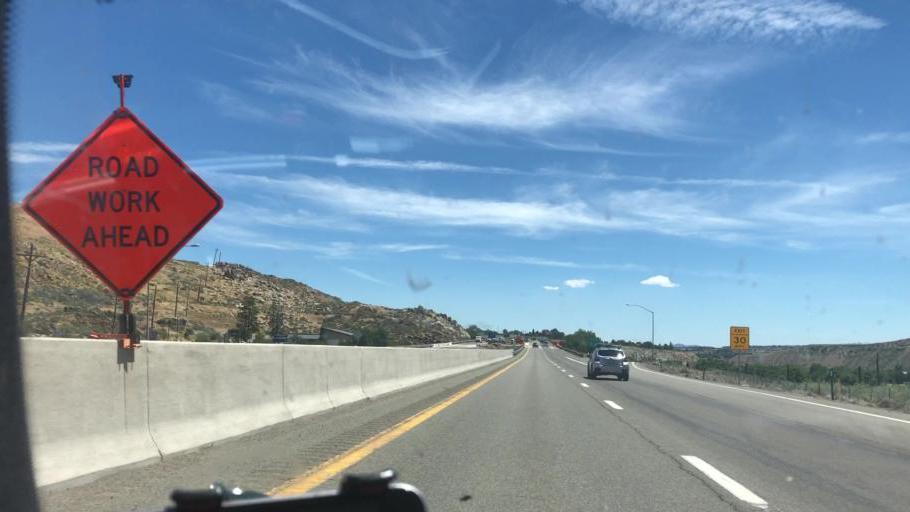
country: US
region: Nevada
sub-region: Washoe County
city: Mogul
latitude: 39.5153
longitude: -119.9180
